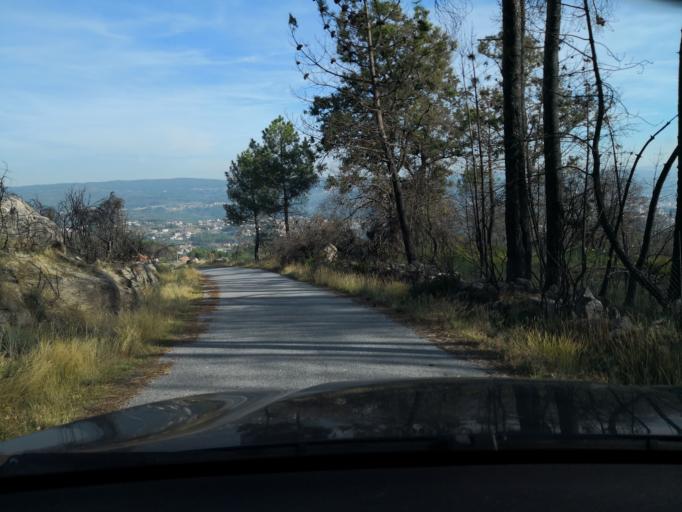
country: PT
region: Vila Real
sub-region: Vila Real
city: Vila Real
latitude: 41.3409
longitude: -7.7544
